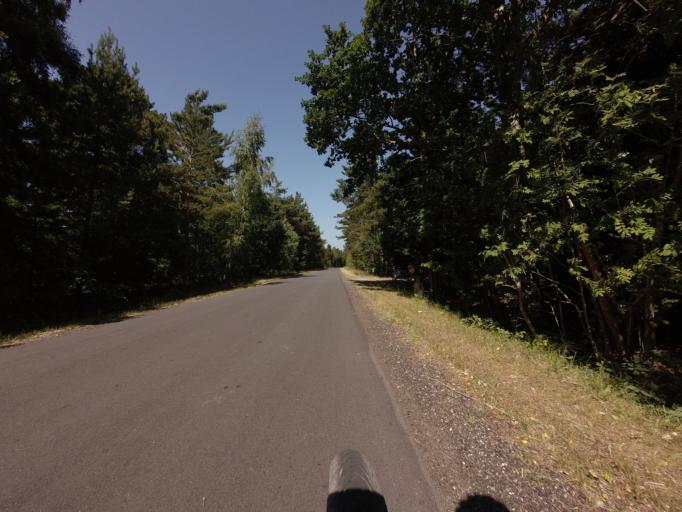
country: DK
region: North Denmark
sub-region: Laeso Kommune
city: Byrum
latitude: 57.2628
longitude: 11.0008
